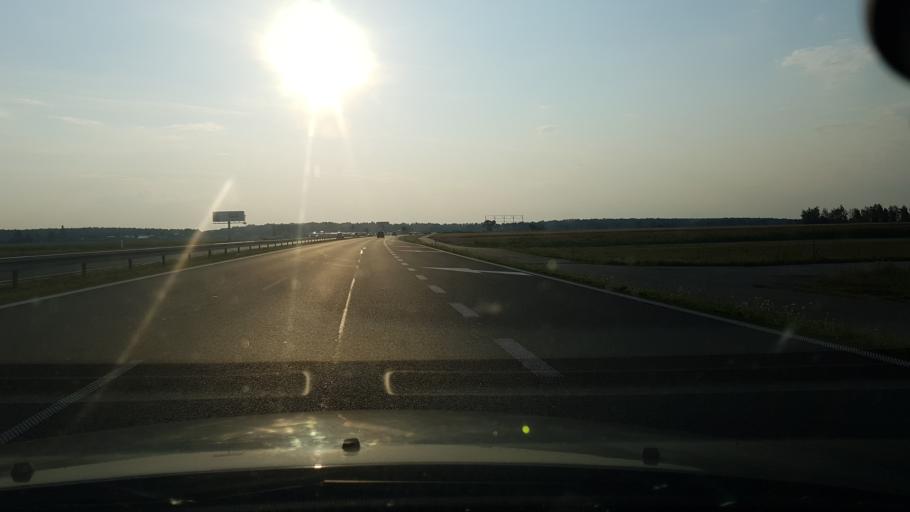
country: PL
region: Masovian Voivodeship
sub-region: Powiat nowodworski
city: Zakroczym
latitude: 52.4457
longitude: 20.6089
